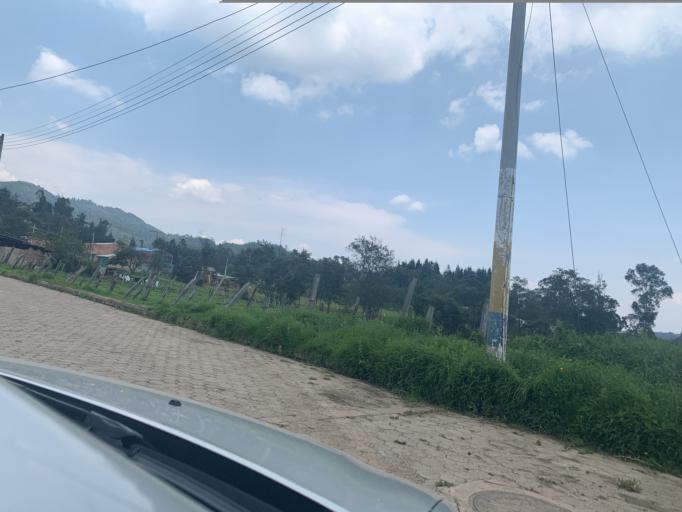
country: CO
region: Boyaca
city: Raquira
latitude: 5.5179
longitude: -73.7203
